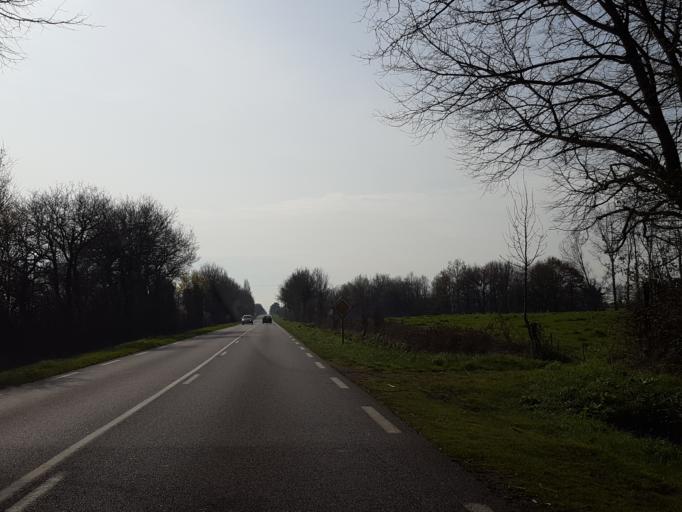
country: FR
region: Pays de la Loire
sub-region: Departement de la Vendee
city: Les Lucs-sur-Boulogne
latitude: 46.8370
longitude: -1.4877
